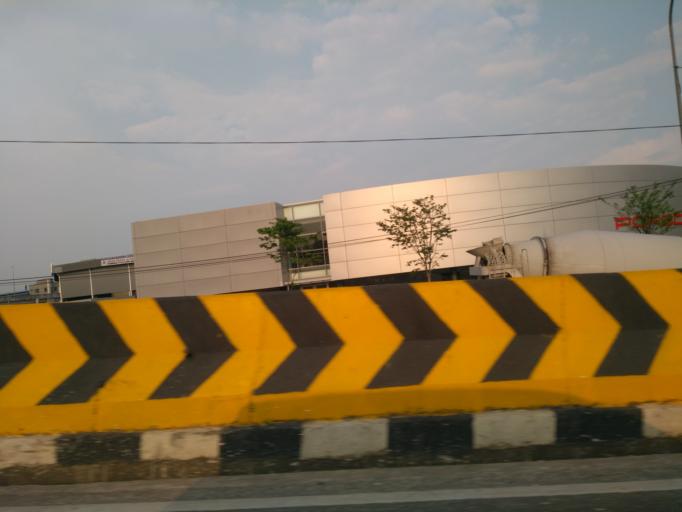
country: MY
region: Kuala Lumpur
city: Kuala Lumpur
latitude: 3.1207
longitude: 101.7084
